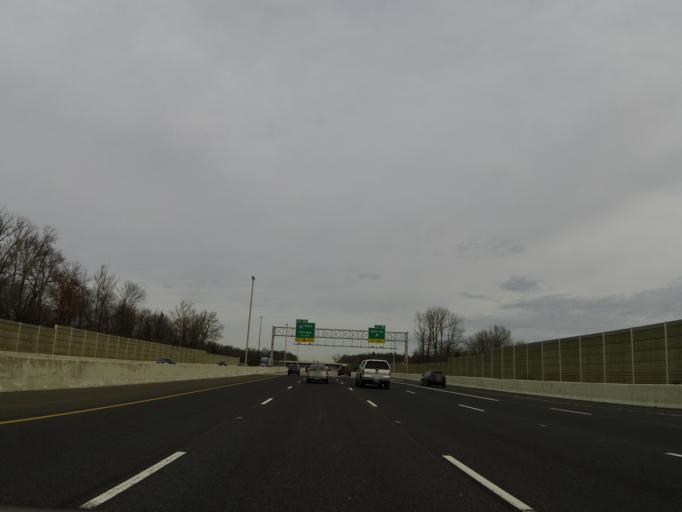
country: US
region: Indiana
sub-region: Marion County
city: Speedway
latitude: 39.8477
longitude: -86.2761
